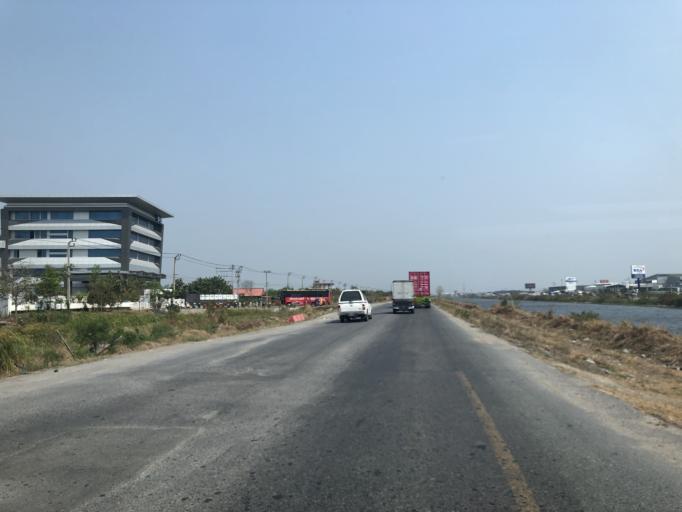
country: TH
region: Samut Prakan
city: Bang Bo District
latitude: 13.5586
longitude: 100.7539
